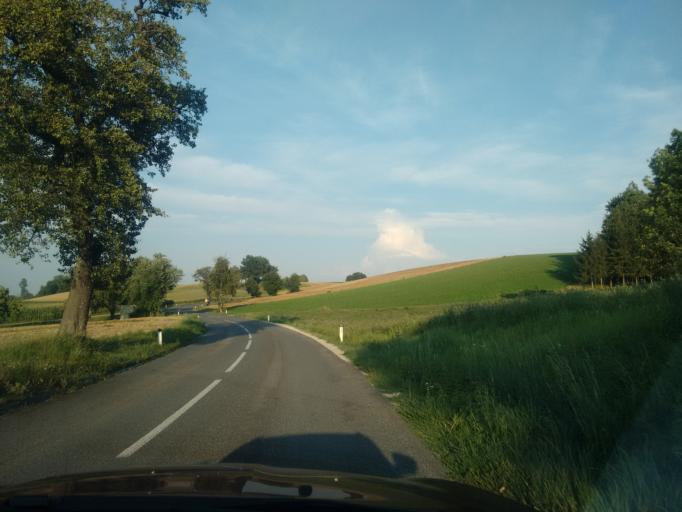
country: AT
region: Upper Austria
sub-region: Politischer Bezirk Vocklabruck
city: Wolfsegg am Hausruck
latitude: 48.1421
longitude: 13.7118
